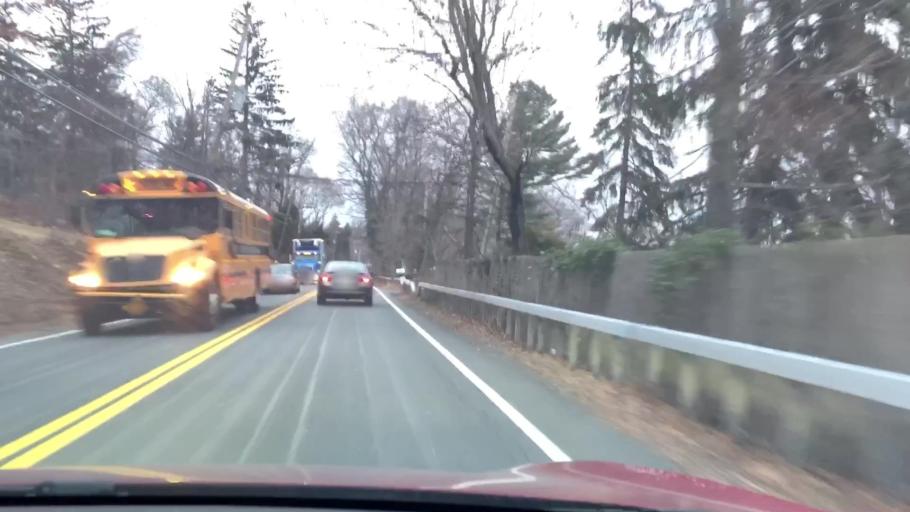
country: US
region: New York
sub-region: Rockland County
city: South Nyack
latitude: 41.0673
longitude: -73.9233
